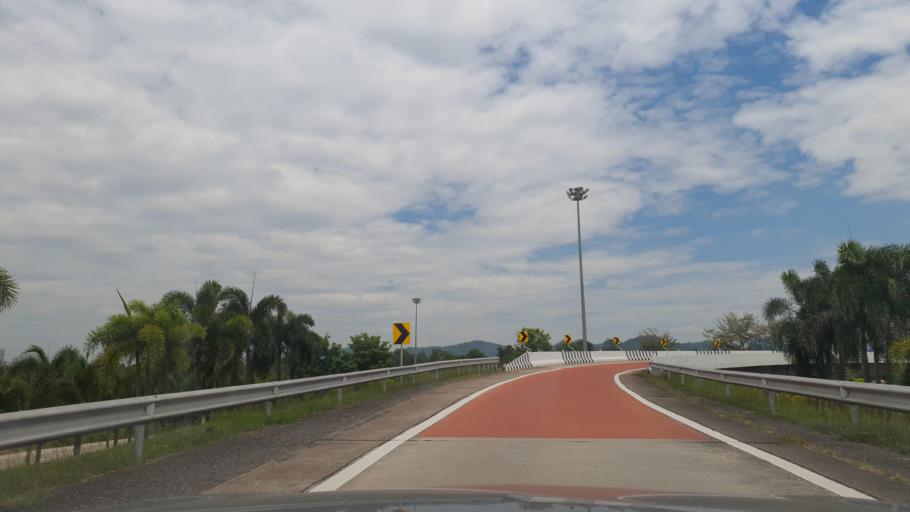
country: TH
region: Chon Buri
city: Bang Lamung
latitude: 12.9680
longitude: 100.9795
